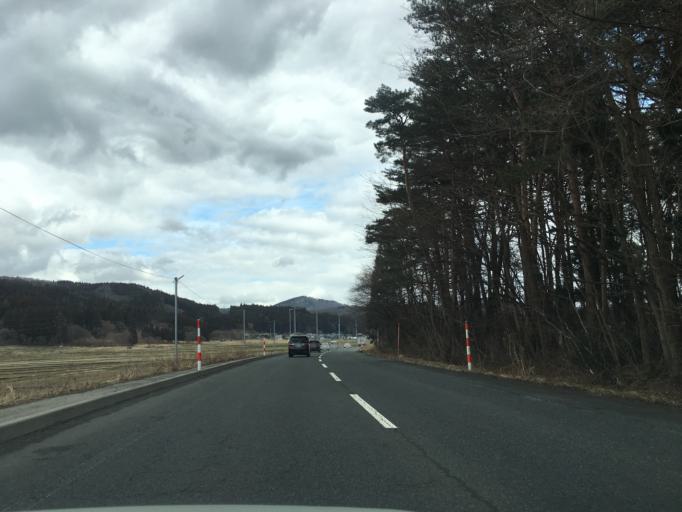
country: JP
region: Akita
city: Hanawa
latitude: 40.2308
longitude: 140.6827
